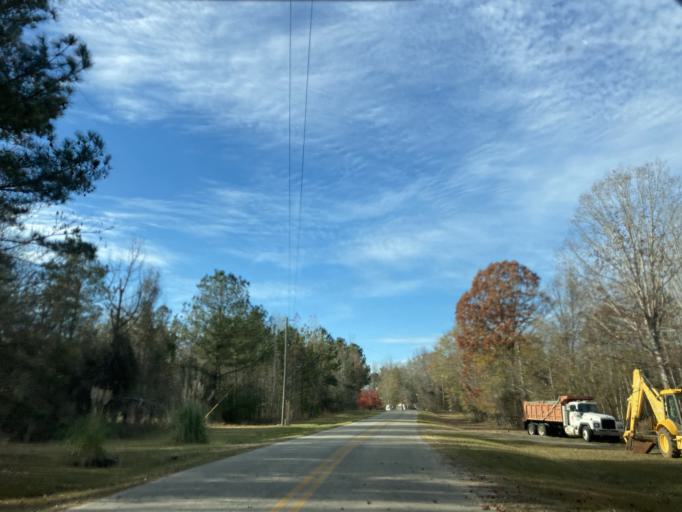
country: US
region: Georgia
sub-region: Jones County
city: Gray
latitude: 32.9085
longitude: -83.5100
